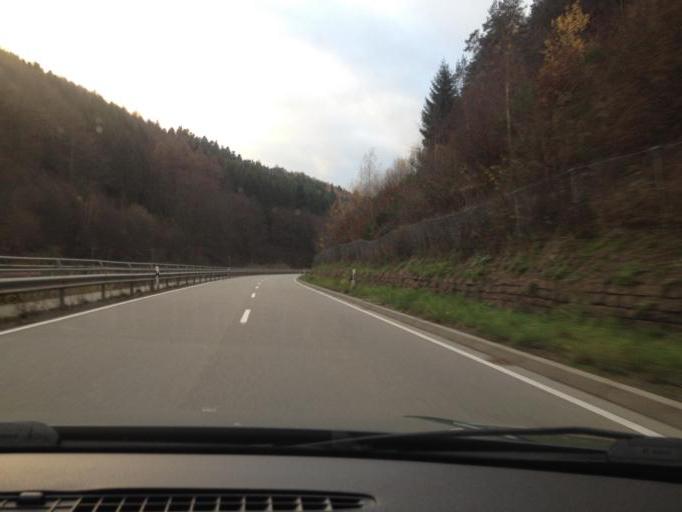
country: DE
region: Rheinland-Pfalz
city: Frankenstein
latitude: 49.4376
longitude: 7.9584
